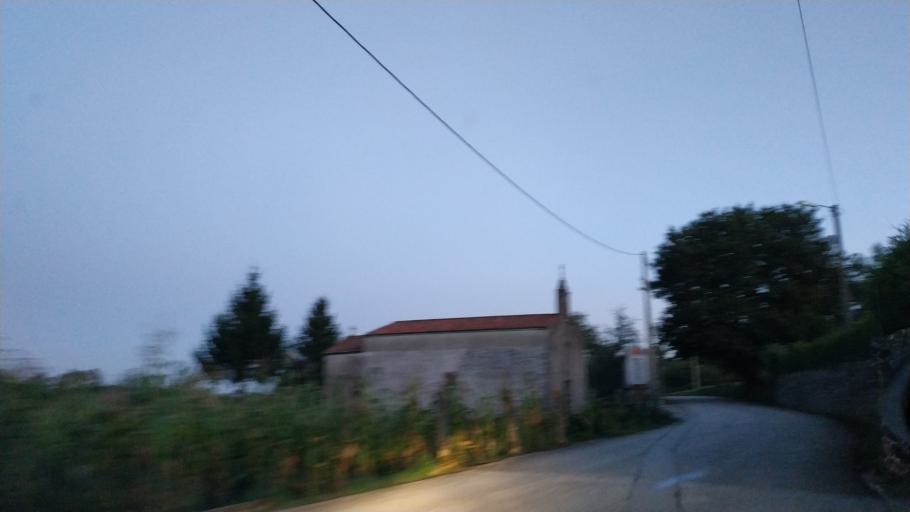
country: ES
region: Galicia
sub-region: Provincia da Coruna
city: Negreira
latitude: 42.9121
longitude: -8.7645
